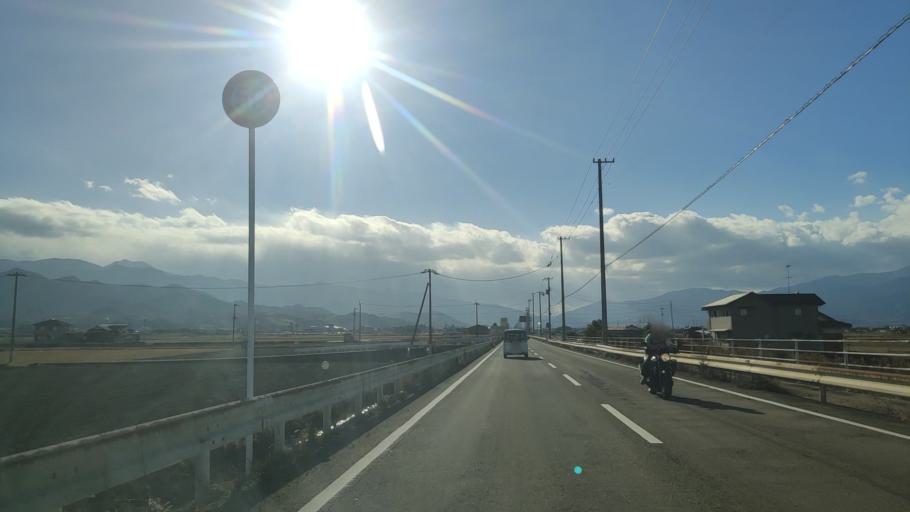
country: JP
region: Ehime
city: Saijo
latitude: 33.9181
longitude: 133.1231
